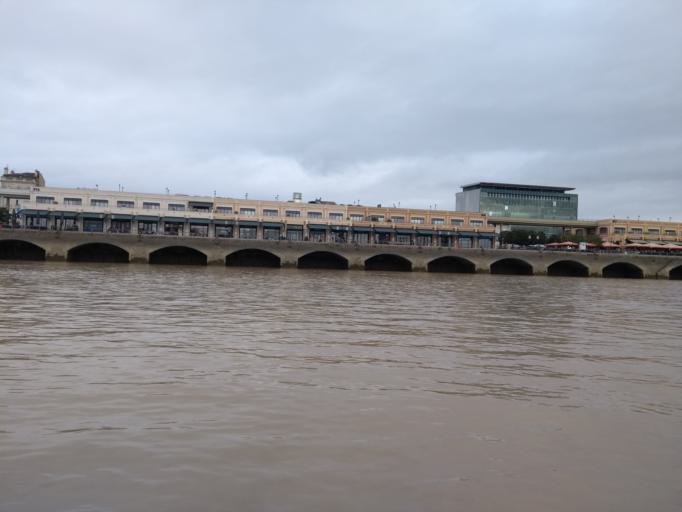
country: FR
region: Aquitaine
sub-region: Departement de la Gironde
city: Bordeaux
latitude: 44.8556
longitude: -0.5598
